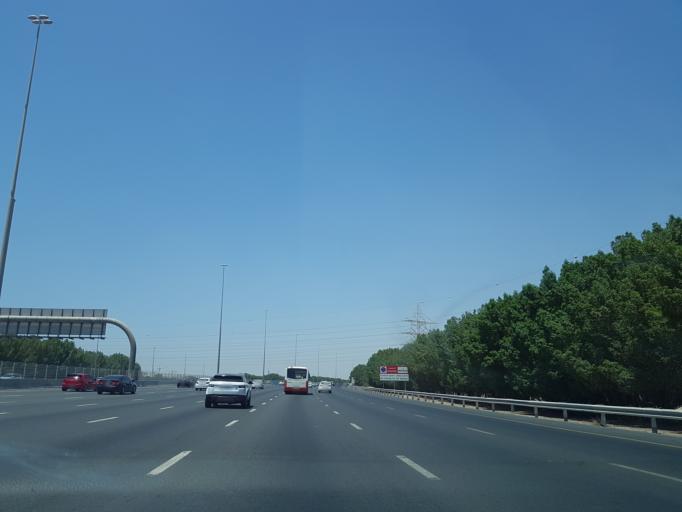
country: AE
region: Ash Shariqah
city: Sharjah
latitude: 25.2594
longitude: 55.4082
